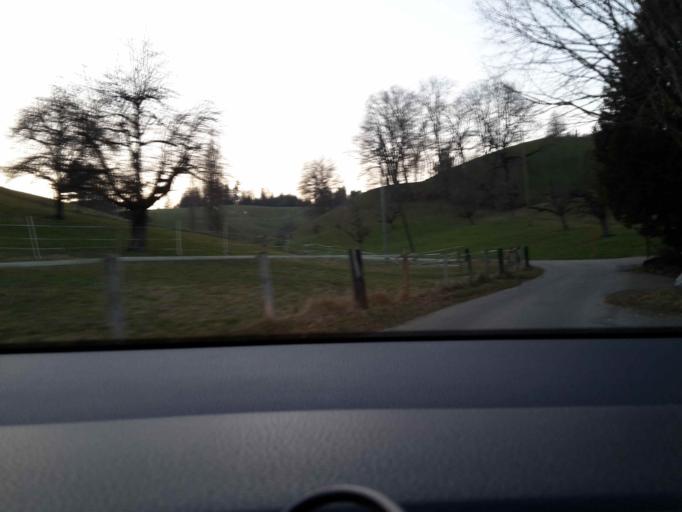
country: CH
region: Bern
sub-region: Oberaargau
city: Rohrbach
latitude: 47.1203
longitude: 7.7991
